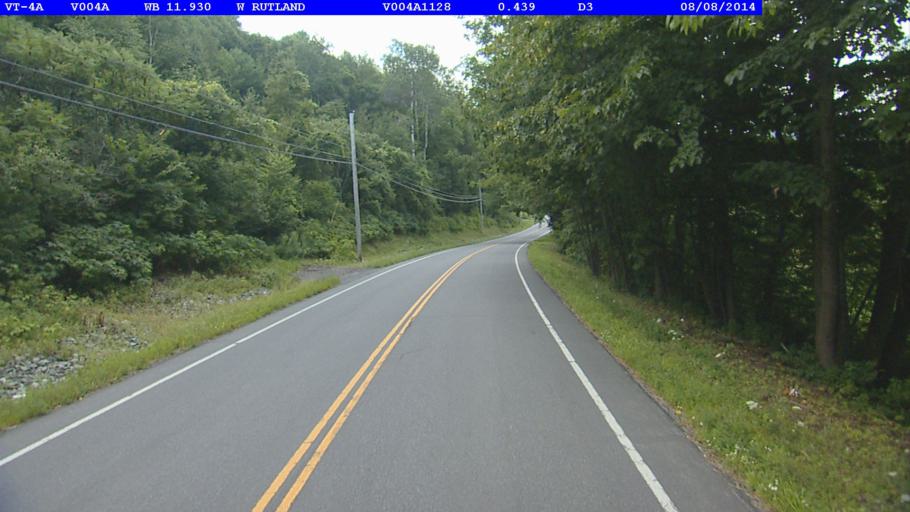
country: US
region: Vermont
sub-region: Rutland County
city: West Rutland
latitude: 43.6046
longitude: -73.0802
